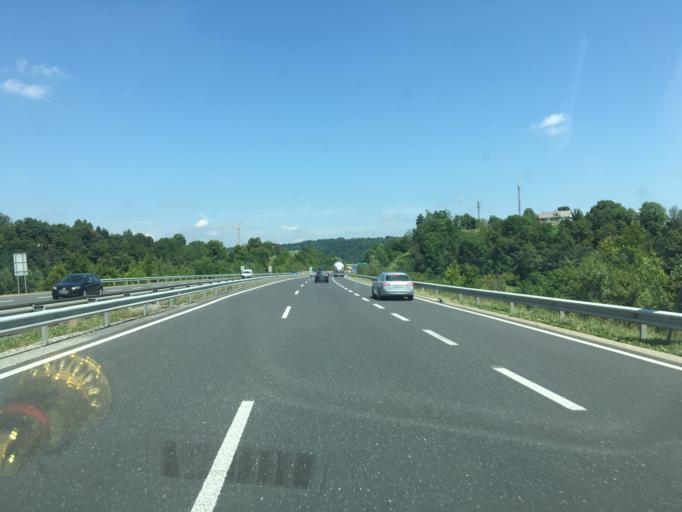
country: SI
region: Sentilj
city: Sentilj v Slov. Goricah
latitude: 46.6719
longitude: 15.6456
